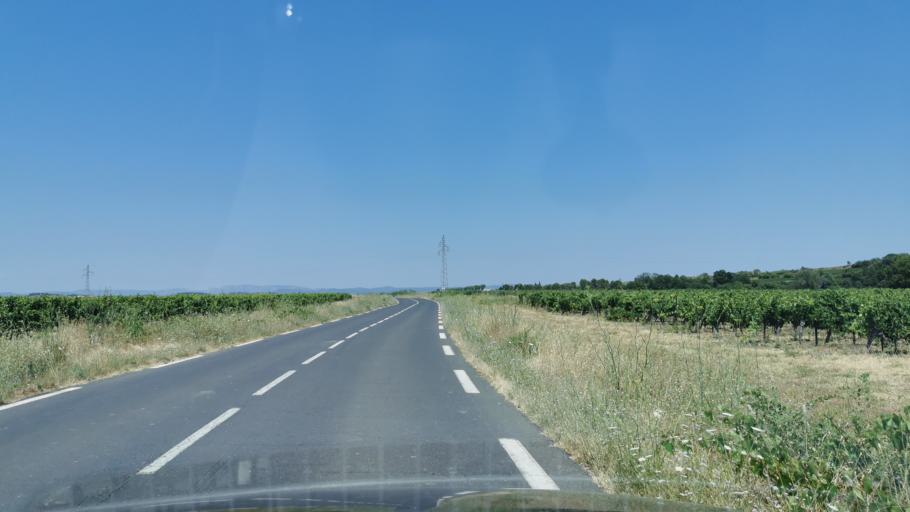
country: FR
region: Languedoc-Roussillon
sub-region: Departement de l'Herault
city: Maureilhan
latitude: 43.3698
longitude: 3.1140
